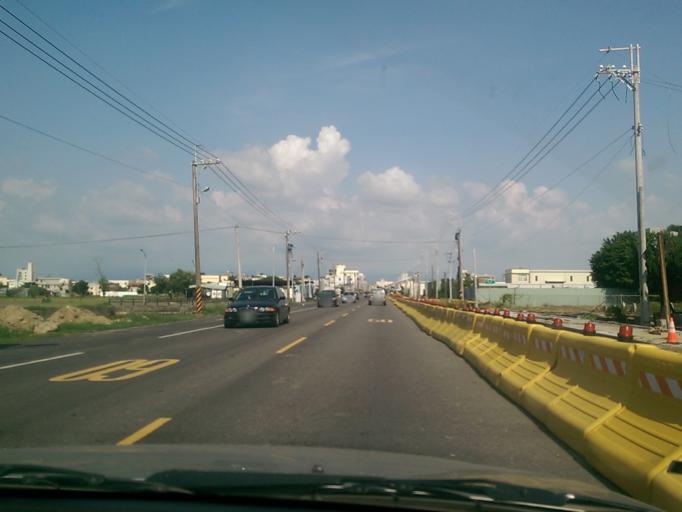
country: TW
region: Taiwan
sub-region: Chiayi
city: Taibao
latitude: 23.5584
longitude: 120.3372
